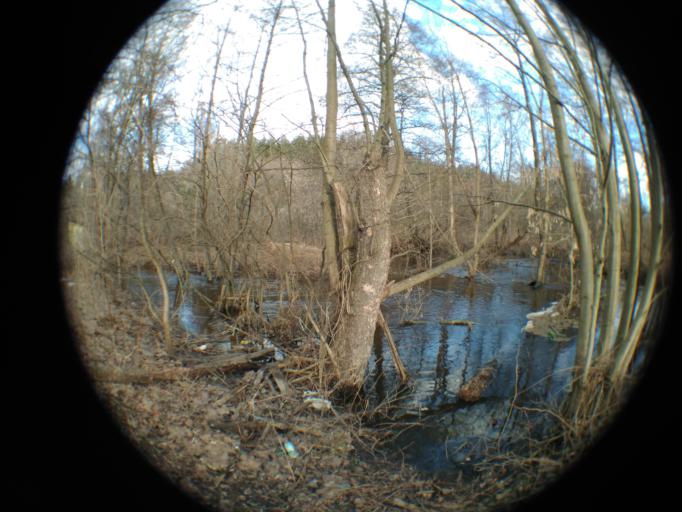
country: RU
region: Moskovskaya
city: Kratovo
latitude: 55.5705
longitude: 38.1700
